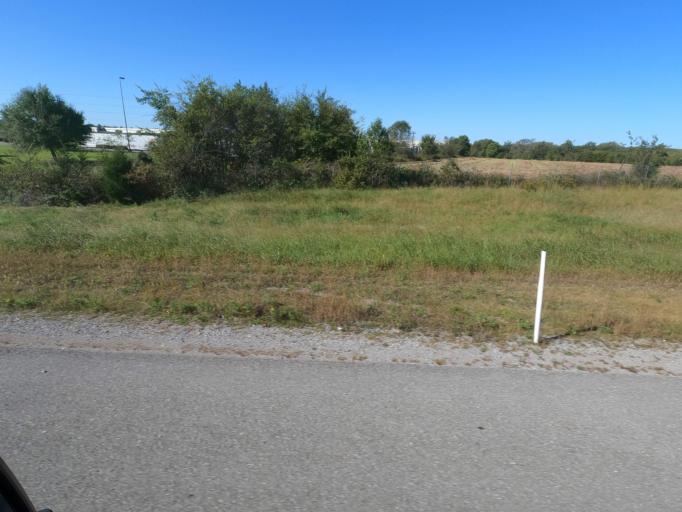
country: US
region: Tennessee
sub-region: Wilson County
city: Rural Hill
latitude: 36.0674
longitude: -86.4315
